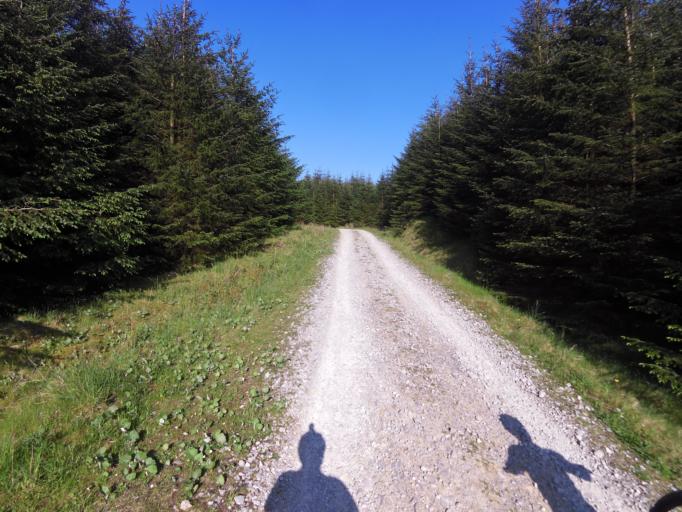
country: GB
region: England
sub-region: North Yorkshire
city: Settle
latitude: 54.0304
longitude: -2.3718
